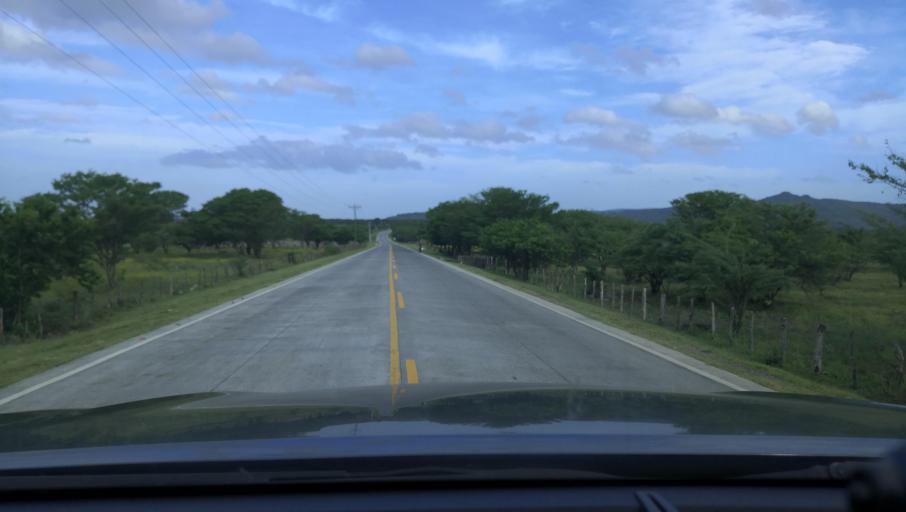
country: NI
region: Boaco
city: San Lorenzo
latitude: 12.1967
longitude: -85.6788
